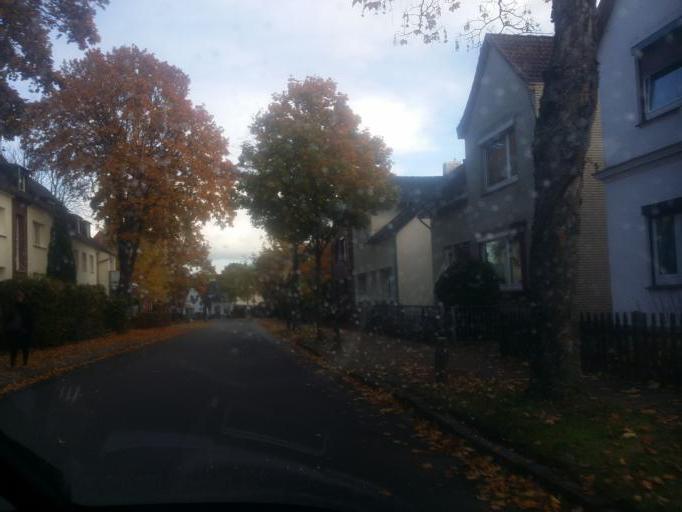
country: DE
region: Schleswig-Holstein
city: Pinneberg
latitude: 53.6548
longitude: 9.7831
